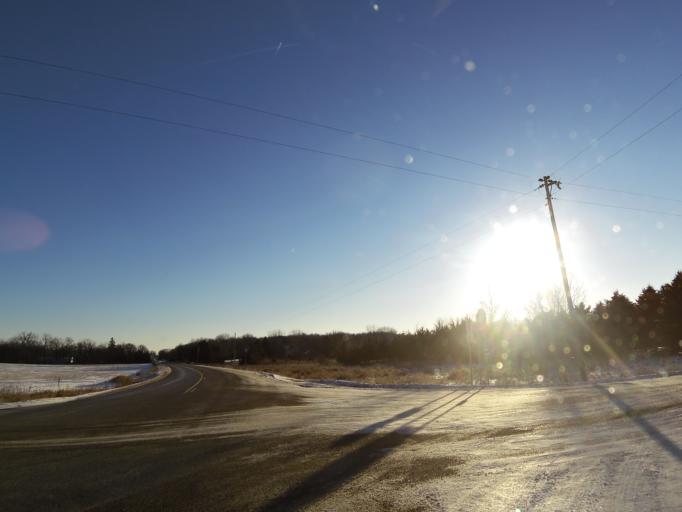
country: US
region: Minnesota
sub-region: Scott County
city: Jordan
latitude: 44.6525
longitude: -93.5163
